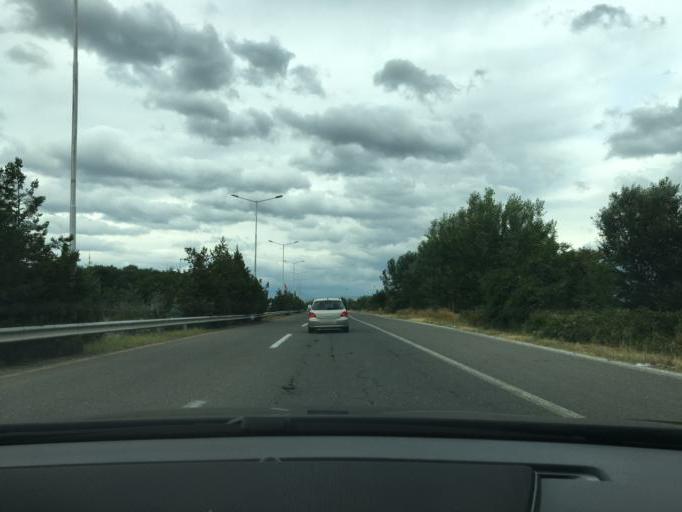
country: MK
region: Ilinden
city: Jurumleri
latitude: 41.9952
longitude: 21.5305
